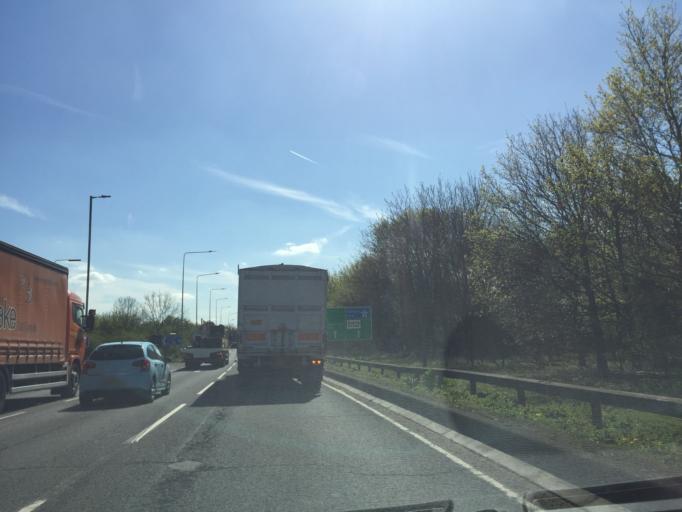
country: GB
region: England
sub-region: Essex
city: Harlow
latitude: 51.7444
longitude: 0.1360
